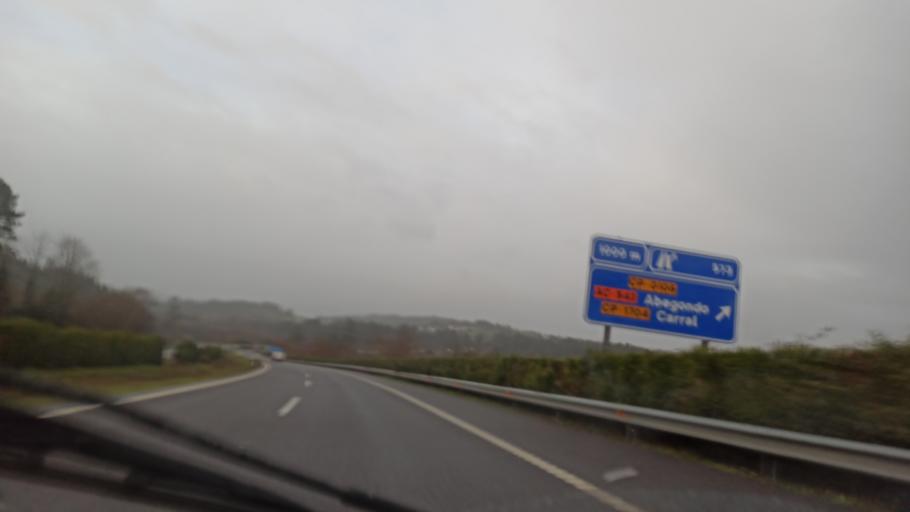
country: ES
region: Galicia
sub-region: Provincia da Coruna
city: Abegondo
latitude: 43.2512
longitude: -8.2805
